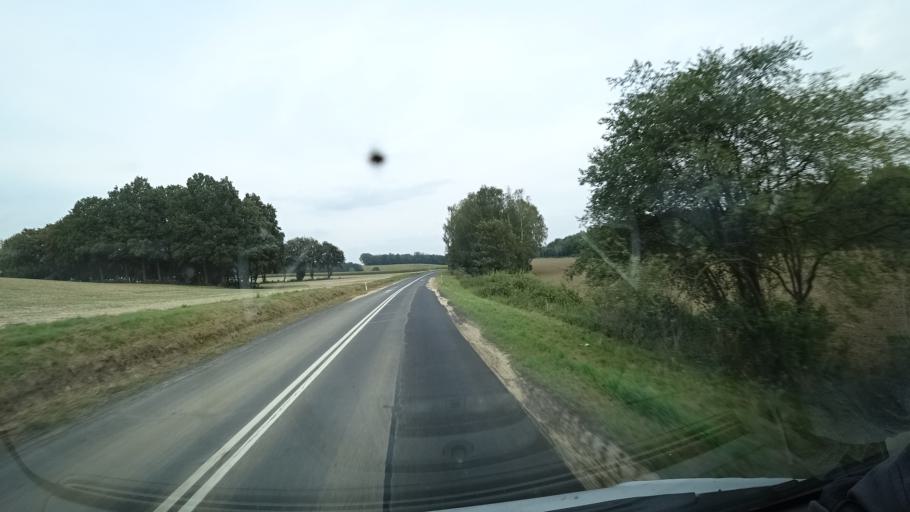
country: PL
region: Silesian Voivodeship
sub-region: Powiat gliwicki
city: Rudziniec
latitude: 50.3962
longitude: 18.4540
